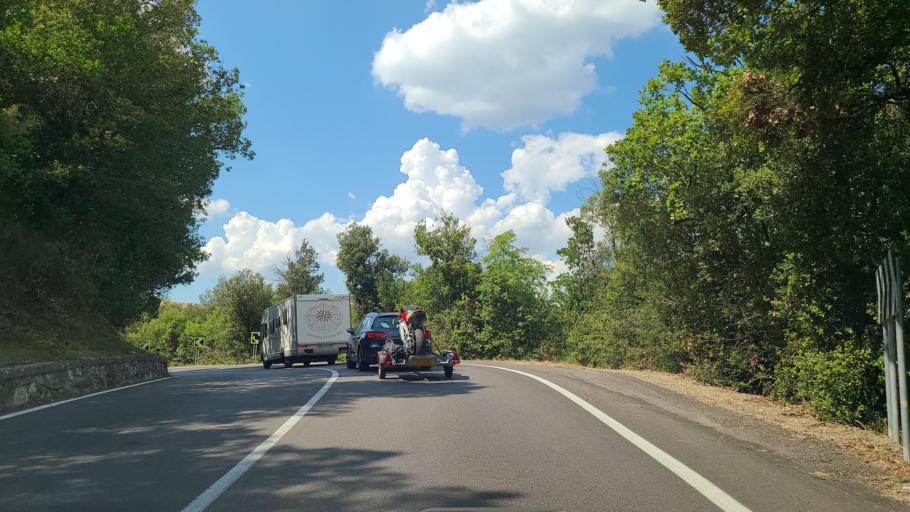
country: IT
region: Tuscany
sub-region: Provincia di Siena
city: San Gimignano
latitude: 43.4023
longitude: 10.9958
